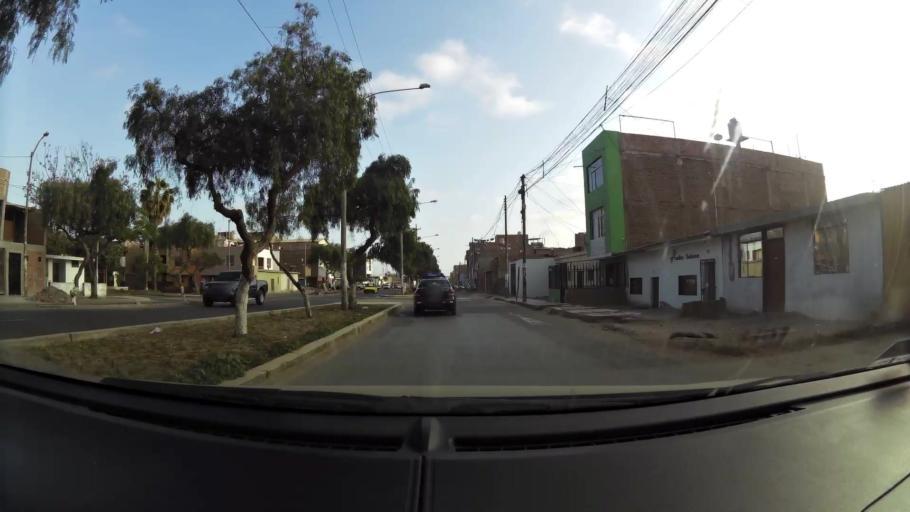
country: PE
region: La Libertad
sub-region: Provincia de Trujillo
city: El Porvenir
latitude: -8.0906
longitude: -79.0133
